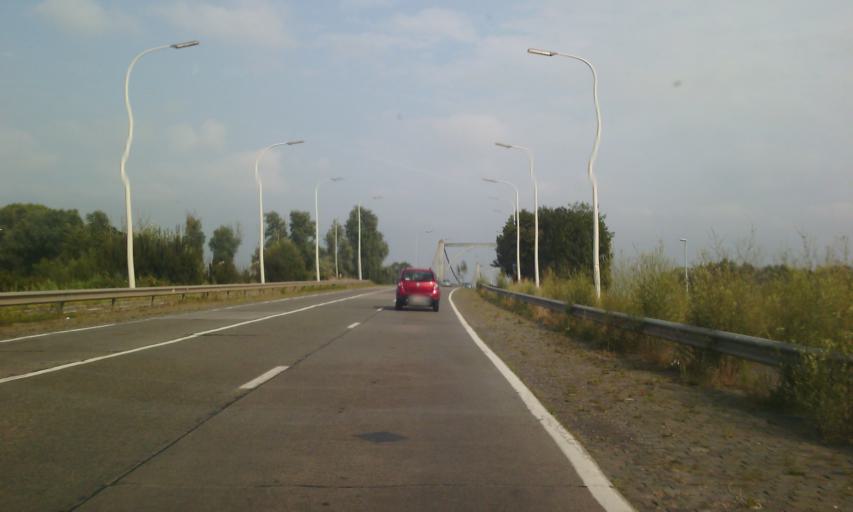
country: BE
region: Flanders
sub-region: Provincie Oost-Vlaanderen
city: Lovendegem
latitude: 51.0888
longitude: 3.6565
